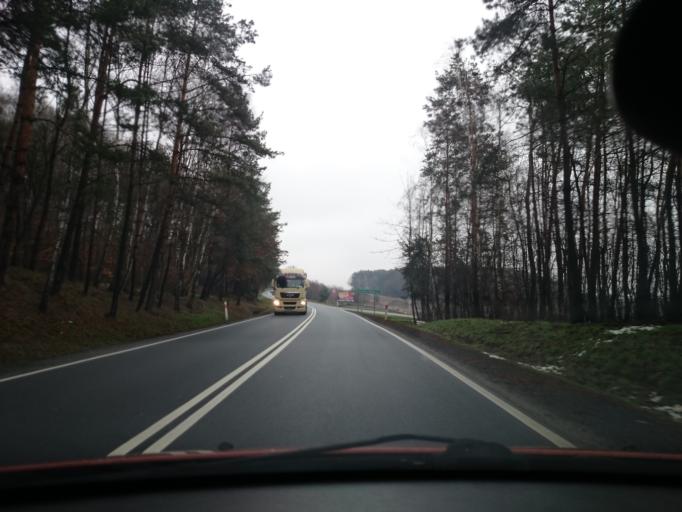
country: PL
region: Opole Voivodeship
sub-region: Powiat nyski
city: Paczkow
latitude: 50.4832
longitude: 16.9893
